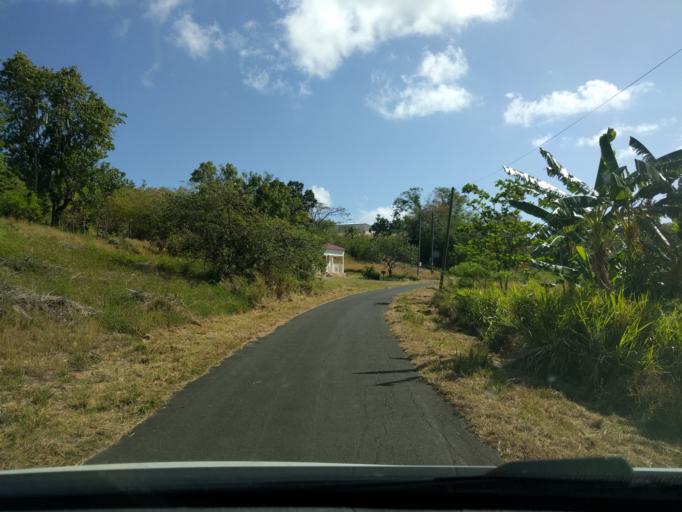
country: GP
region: Guadeloupe
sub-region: Guadeloupe
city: Grand-Bourg
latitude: 15.9754
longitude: -61.2574
